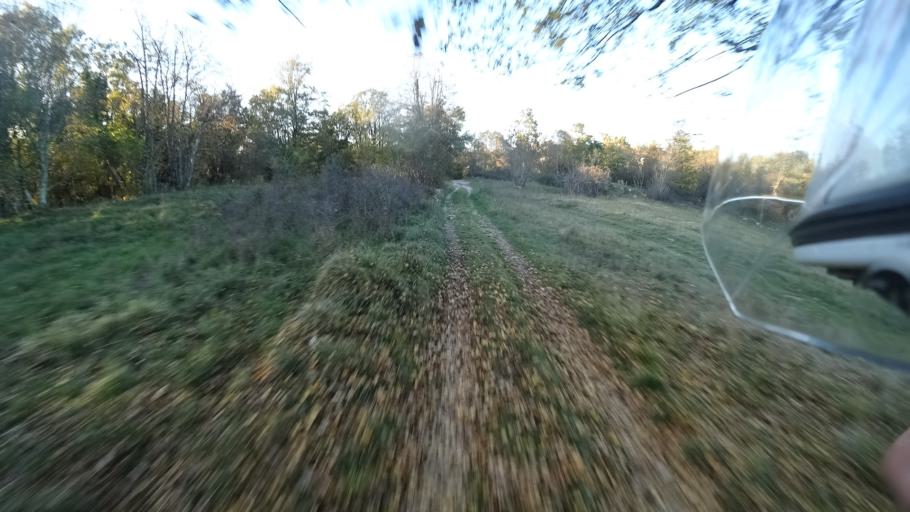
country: HR
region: Primorsko-Goranska
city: Kastav
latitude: 45.4167
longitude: 14.3120
